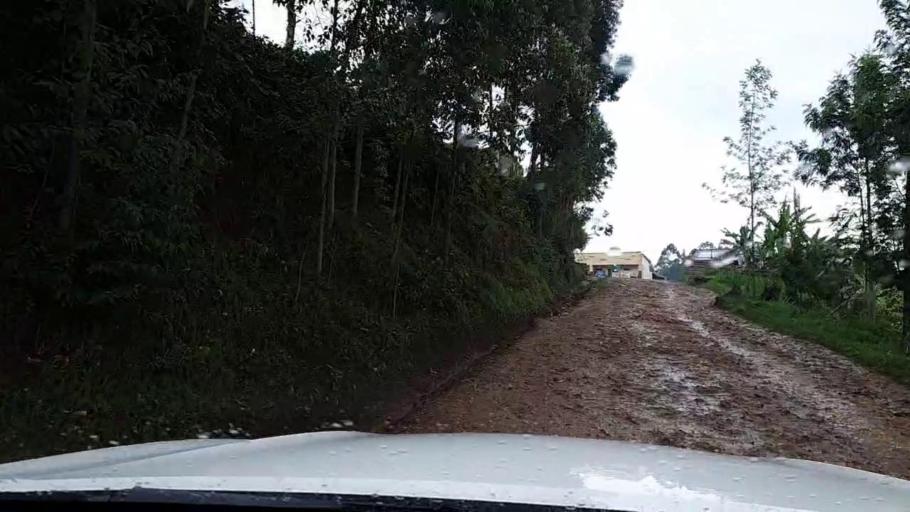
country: RW
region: Western Province
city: Cyangugu
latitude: -2.5444
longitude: 28.9777
